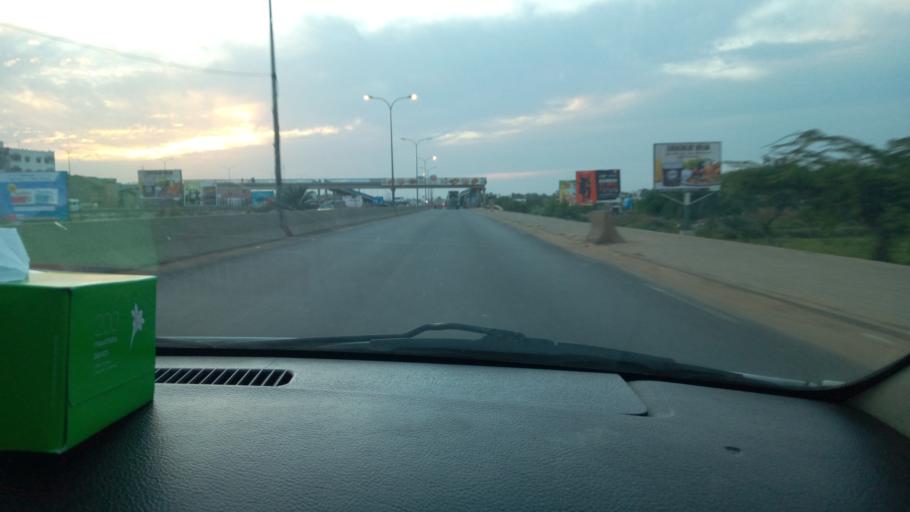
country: SN
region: Dakar
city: Pikine
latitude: 14.7465
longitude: -17.4133
